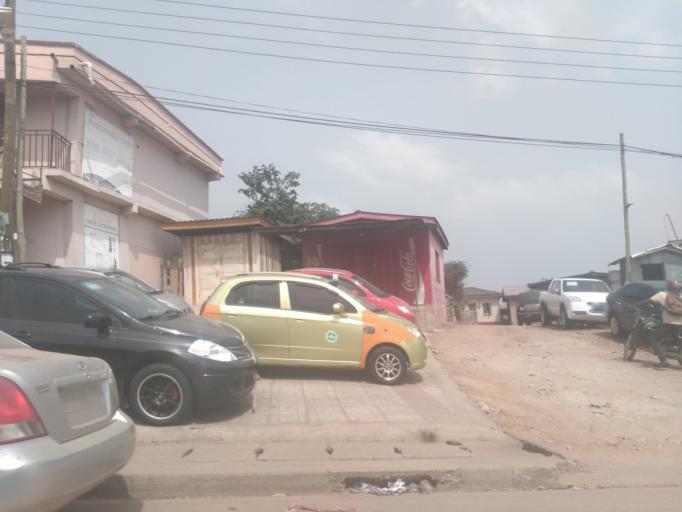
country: GH
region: Greater Accra
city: Dome
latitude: 5.6107
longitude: -0.2342
